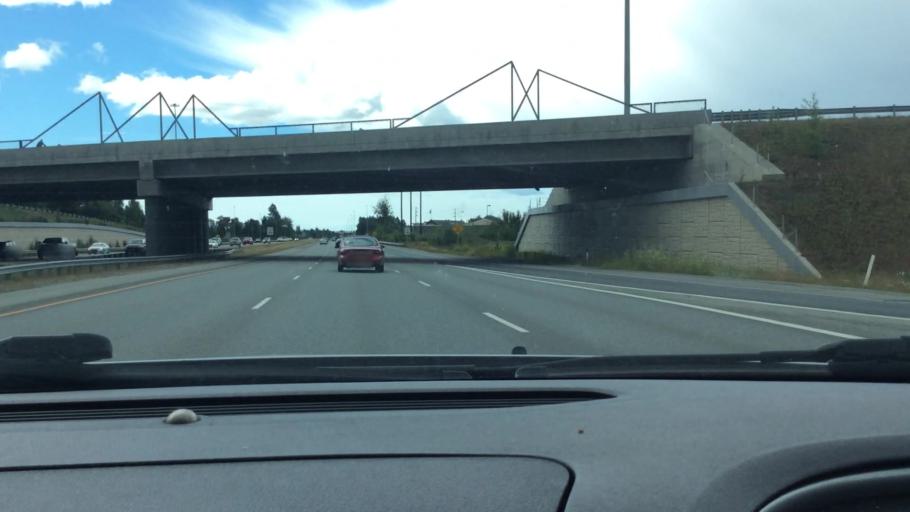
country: US
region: Alaska
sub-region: Anchorage Municipality
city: Anchorage
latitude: 61.2216
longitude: -149.8070
